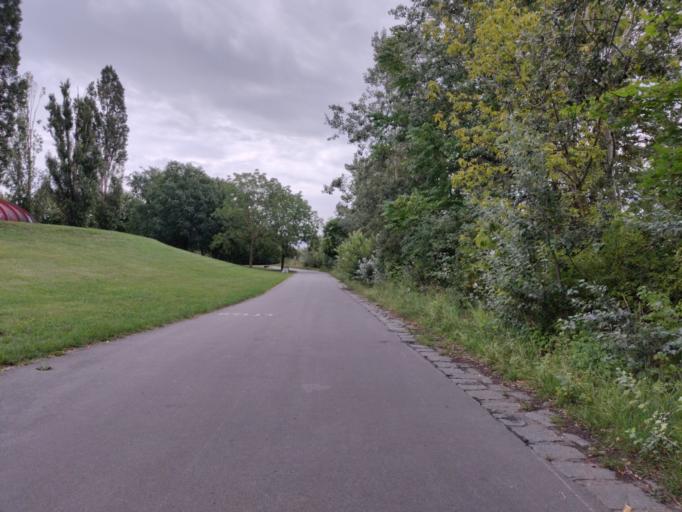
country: AT
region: Vienna
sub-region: Wien Stadt
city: Vienna
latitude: 48.2320
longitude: 16.4038
